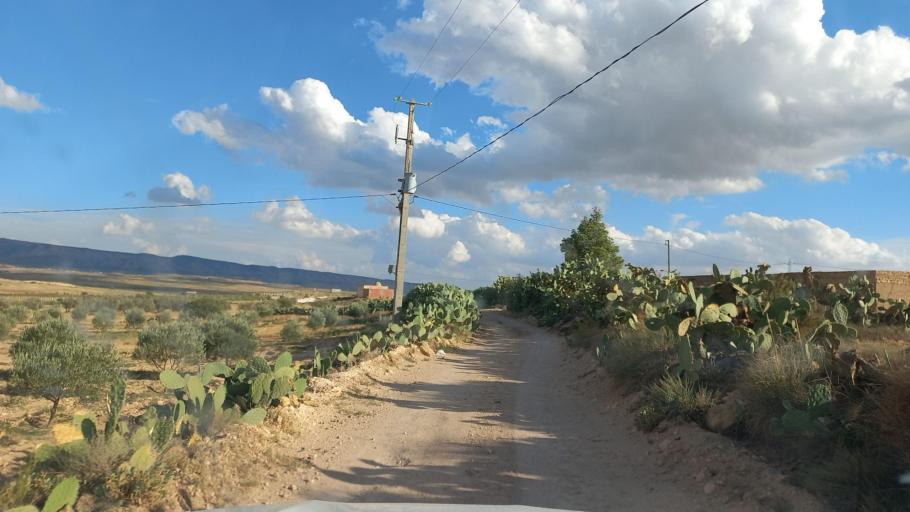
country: TN
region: Al Qasrayn
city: Sbiba
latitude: 35.3815
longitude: 9.0724
